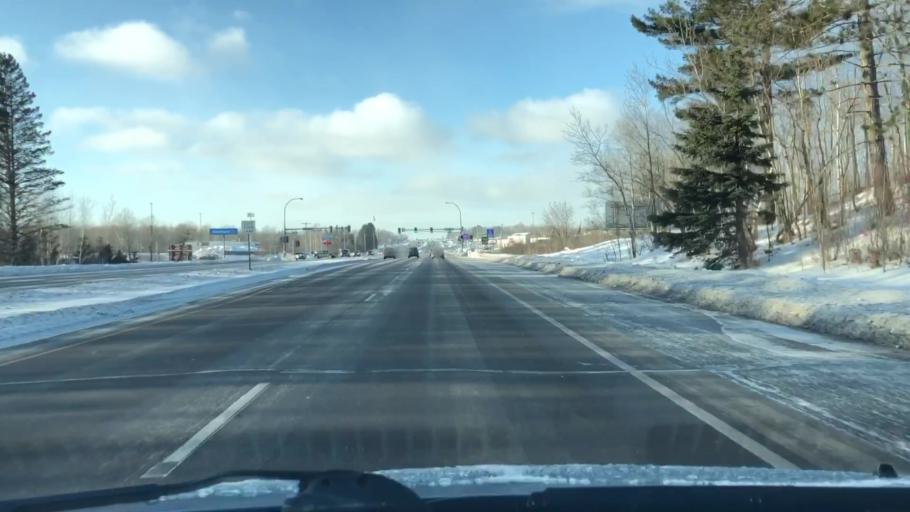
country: US
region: Minnesota
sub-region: Saint Louis County
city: Hermantown
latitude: 46.8181
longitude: -92.1800
